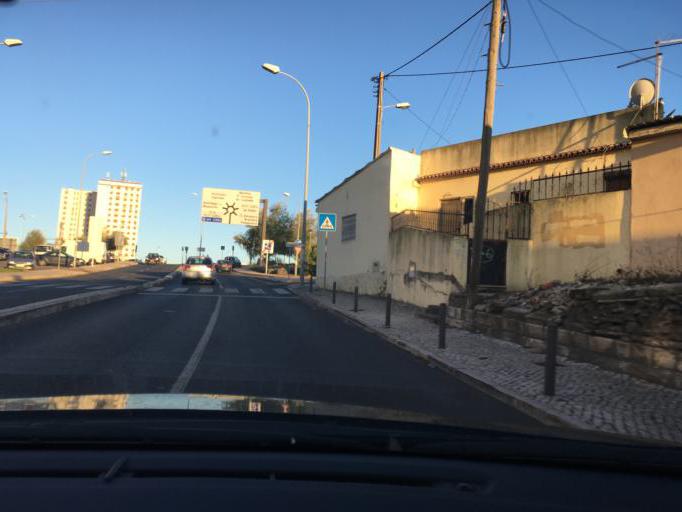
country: PT
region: Lisbon
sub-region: Odivelas
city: Pontinha
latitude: 38.7601
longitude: -9.2027
